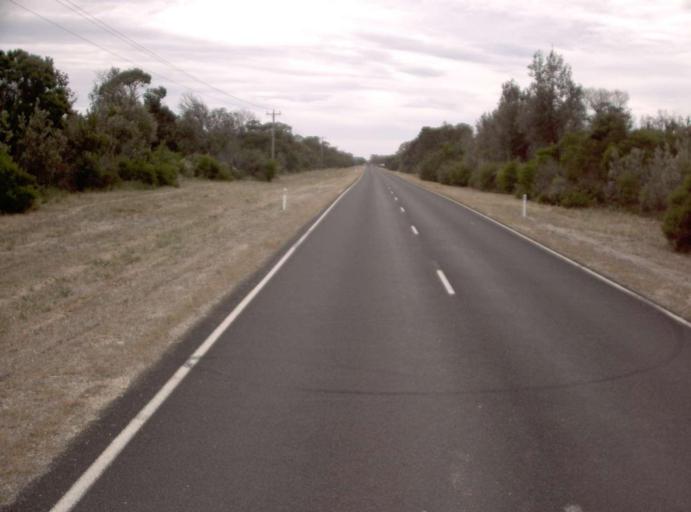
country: AU
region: Victoria
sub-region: East Gippsland
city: Bairnsdale
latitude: -38.0655
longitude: 147.5564
